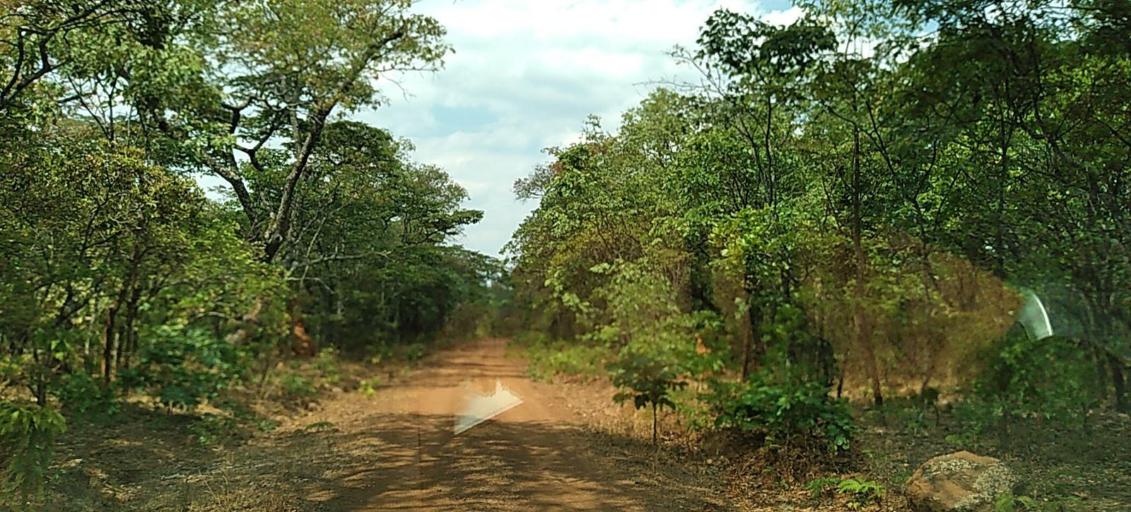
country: ZM
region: Copperbelt
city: Chililabombwe
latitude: -12.4549
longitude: 27.6058
